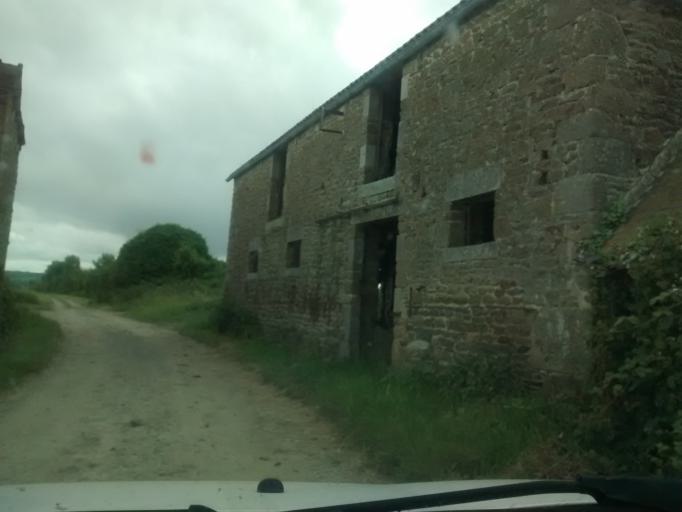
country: FR
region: Brittany
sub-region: Departement d'Ille-et-Vilaine
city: Cherrueix
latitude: 48.6005
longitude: -1.6826
